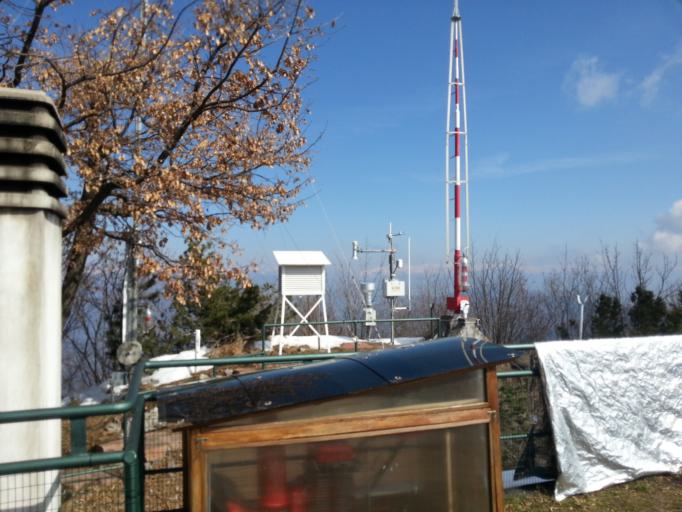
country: IT
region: Lombardy
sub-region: Provincia di Varese
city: Brinzio
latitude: 45.8685
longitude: 8.7703
